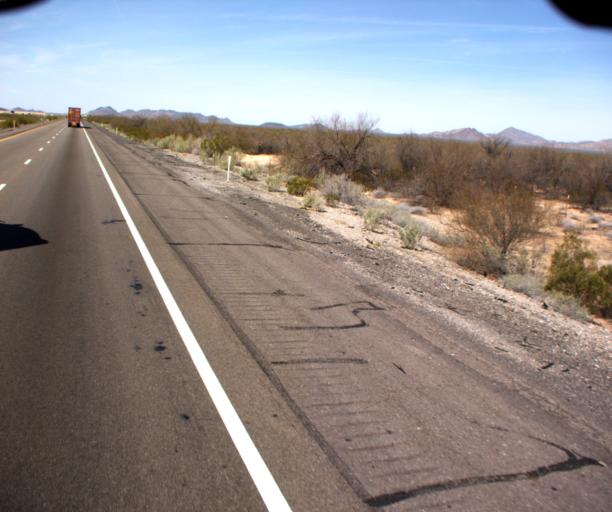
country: US
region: Arizona
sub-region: La Paz County
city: Salome
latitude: 33.5926
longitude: -113.5076
